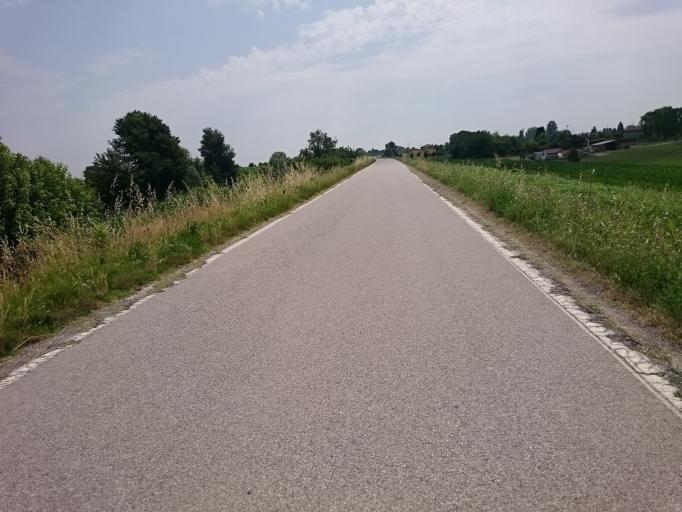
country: IT
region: Veneto
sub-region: Provincia di Padova
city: Codevigo
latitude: 45.2353
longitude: 12.1028
